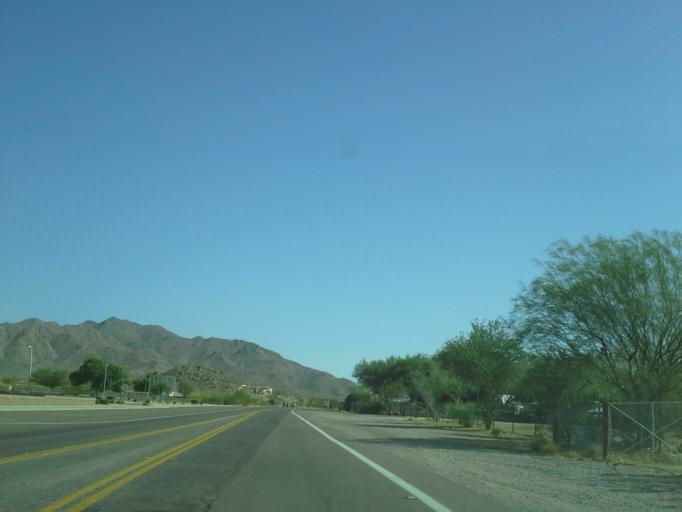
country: US
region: Arizona
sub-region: Maricopa County
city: Queen Creek
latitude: 33.2113
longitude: -111.7205
